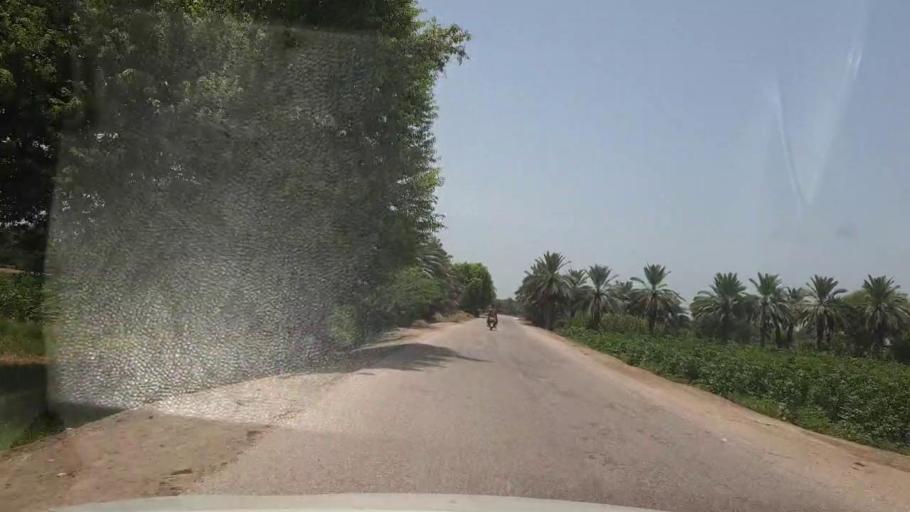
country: PK
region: Sindh
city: Bozdar
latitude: 27.1882
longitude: 68.6050
